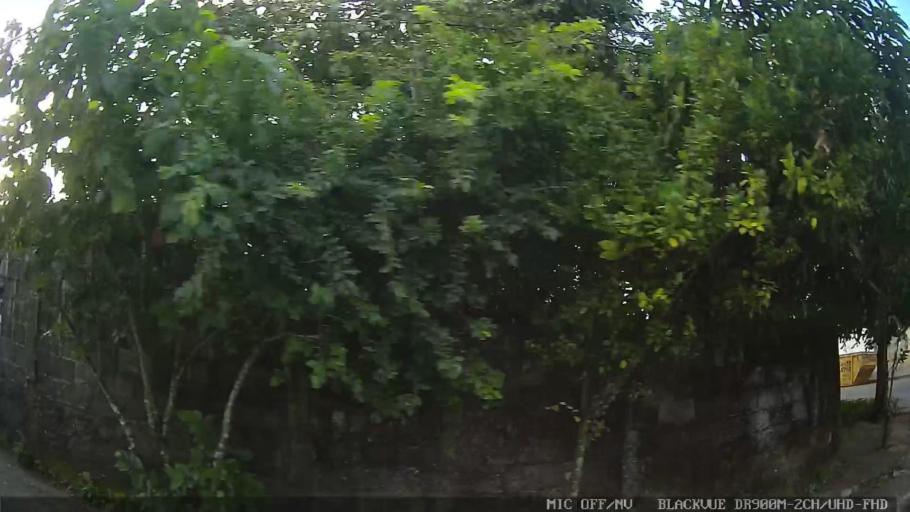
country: BR
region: Sao Paulo
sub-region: Itanhaem
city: Itanhaem
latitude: -24.1858
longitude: -46.8276
